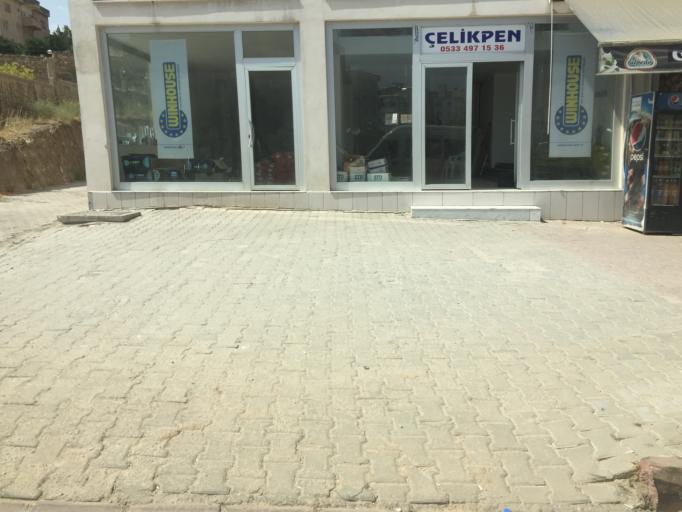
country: TR
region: Mardin
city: Midyat
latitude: 37.4298
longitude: 41.3376
